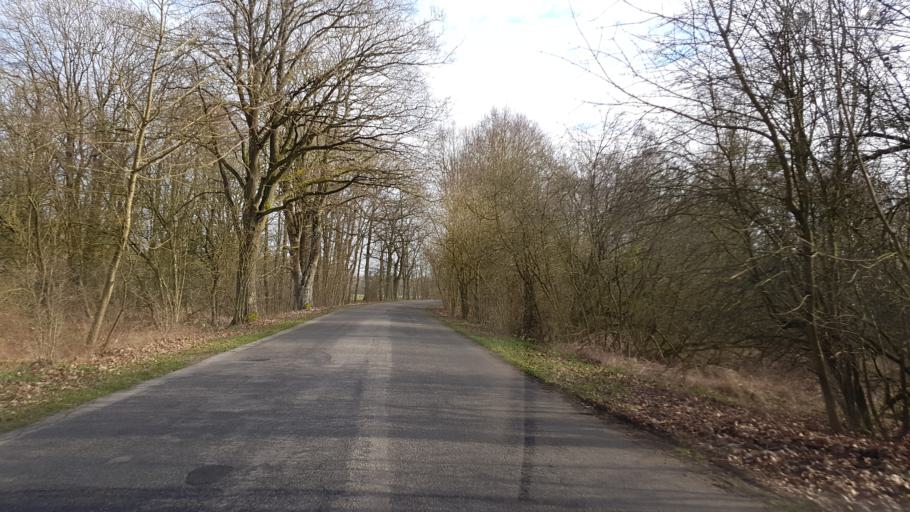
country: PL
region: West Pomeranian Voivodeship
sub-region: Powiat policki
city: Dobra
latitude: 53.5373
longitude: 14.3193
